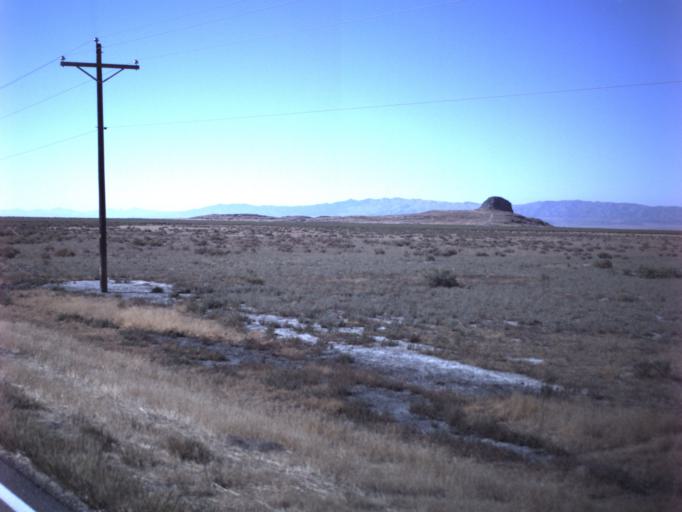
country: US
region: Utah
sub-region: Tooele County
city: Grantsville
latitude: 40.7200
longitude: -112.6604
